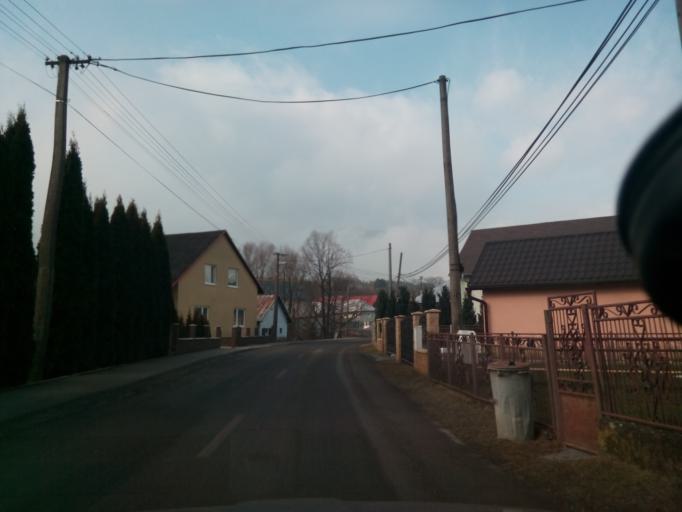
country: SK
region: Presovsky
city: Lipany
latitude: 49.1933
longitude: 20.8261
